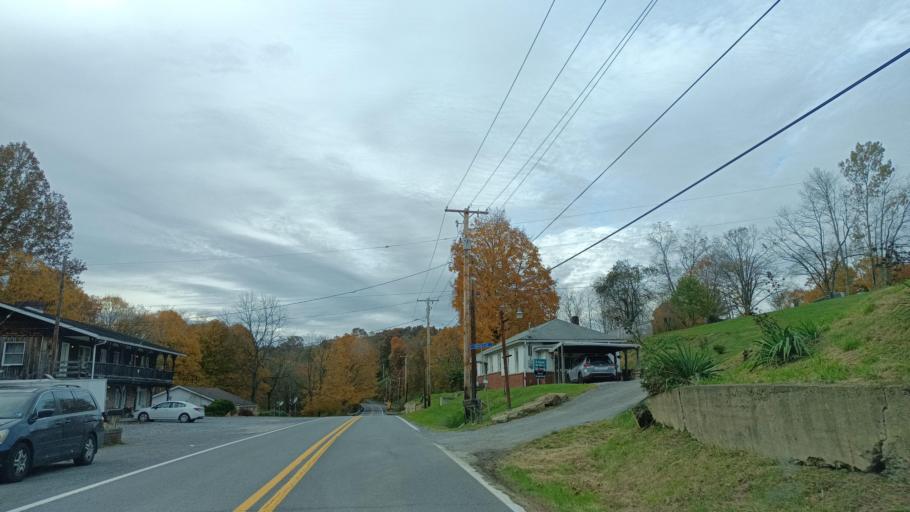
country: US
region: West Virginia
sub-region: Taylor County
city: Grafton
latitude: 39.3340
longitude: -79.8704
